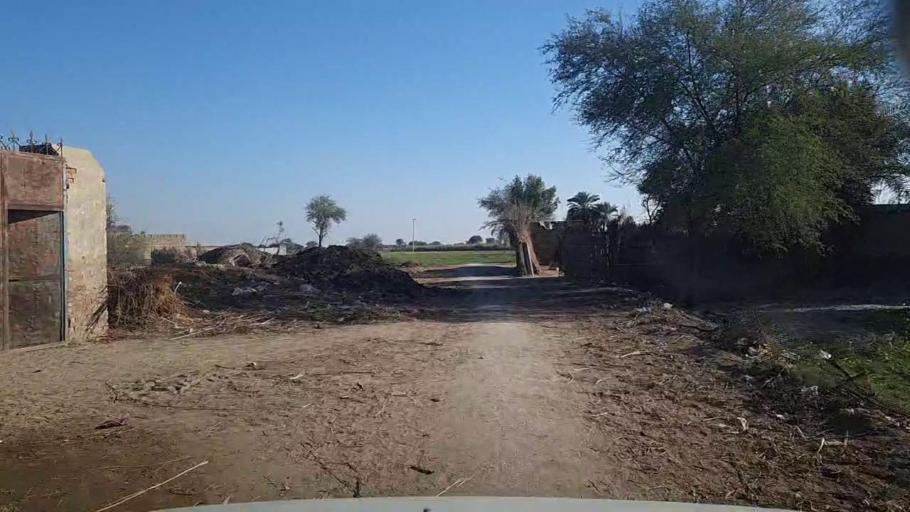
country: PK
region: Sindh
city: Khairpur
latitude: 27.9778
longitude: 69.7685
